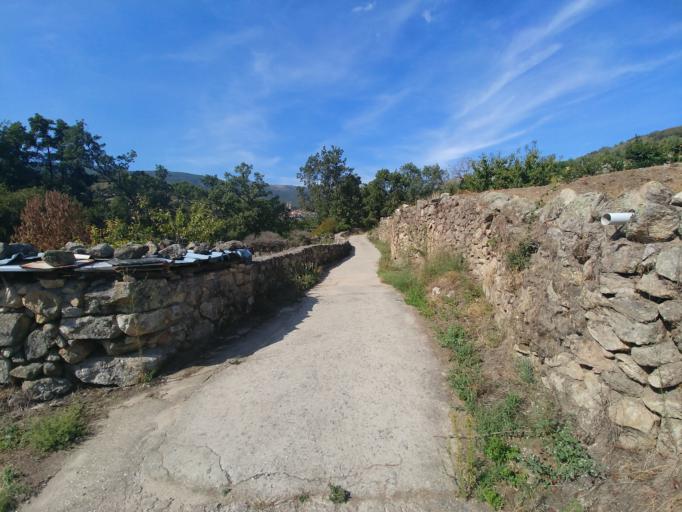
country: ES
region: Extremadura
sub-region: Provincia de Caceres
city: Garganta la Olla
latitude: 40.1065
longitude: -5.7738
